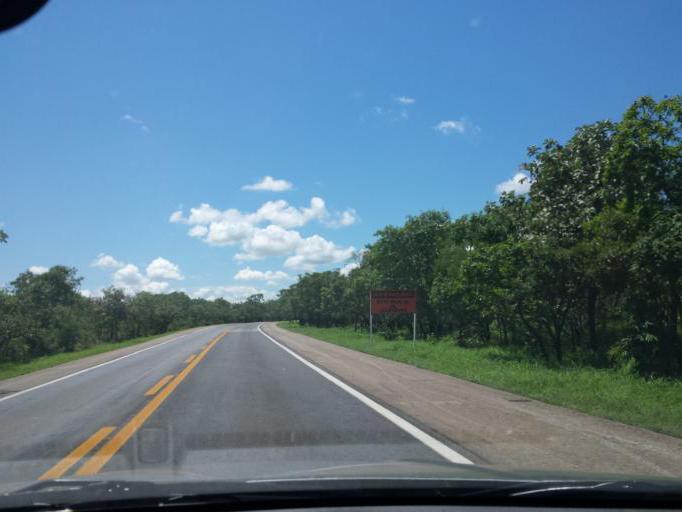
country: BR
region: Goias
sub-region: Luziania
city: Luziania
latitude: -16.4466
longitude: -47.8099
